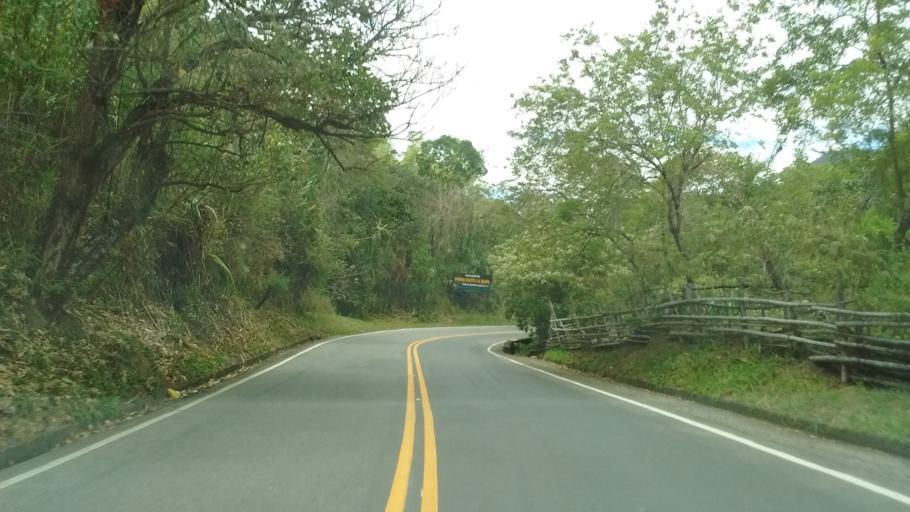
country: CO
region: Cauca
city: Rosas
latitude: 2.2358
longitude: -76.7861
